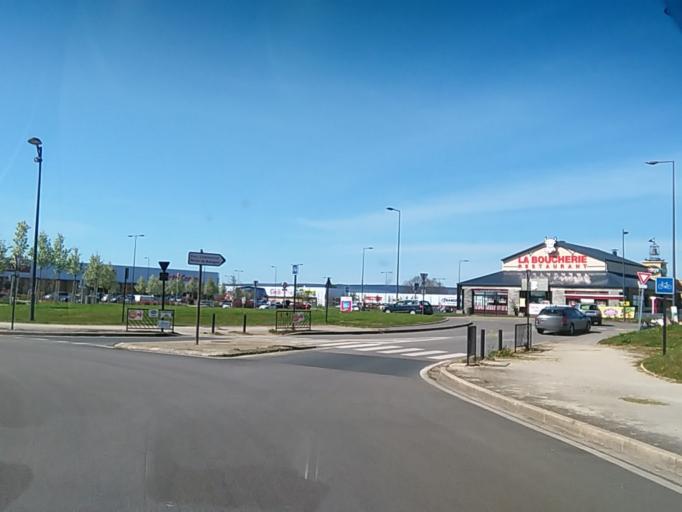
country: FR
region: Lower Normandy
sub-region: Departement de l'Orne
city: Saint-Germain-du-Corbeis
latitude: 48.4332
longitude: 0.0662
